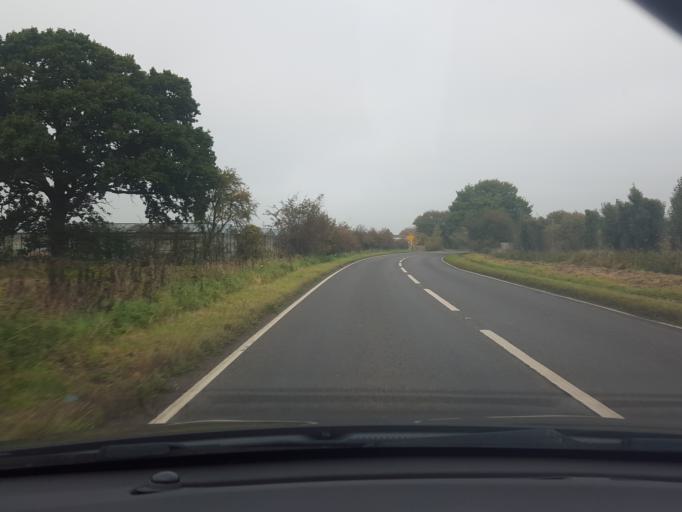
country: GB
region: England
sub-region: Suffolk
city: East Bergholt
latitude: 51.9293
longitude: 0.9929
